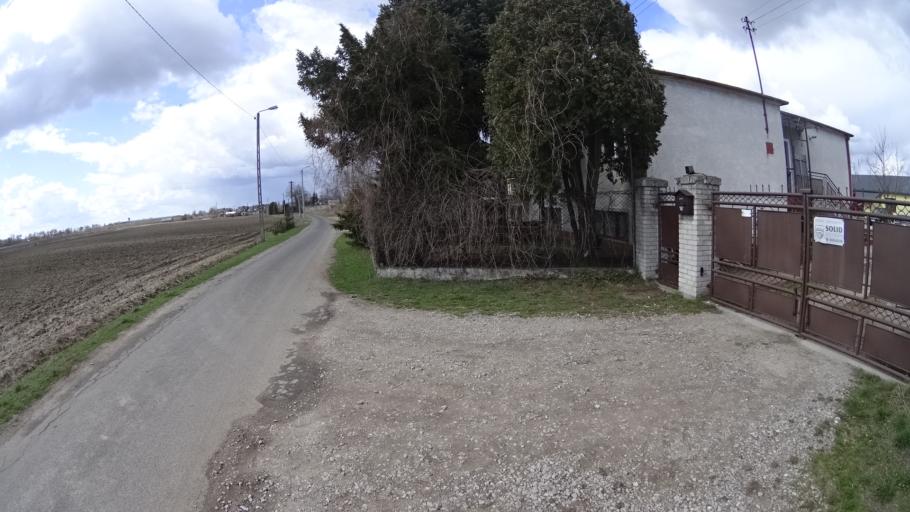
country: PL
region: Masovian Voivodeship
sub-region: Powiat warszawski zachodni
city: Jozefow
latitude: 52.2177
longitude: 20.7292
